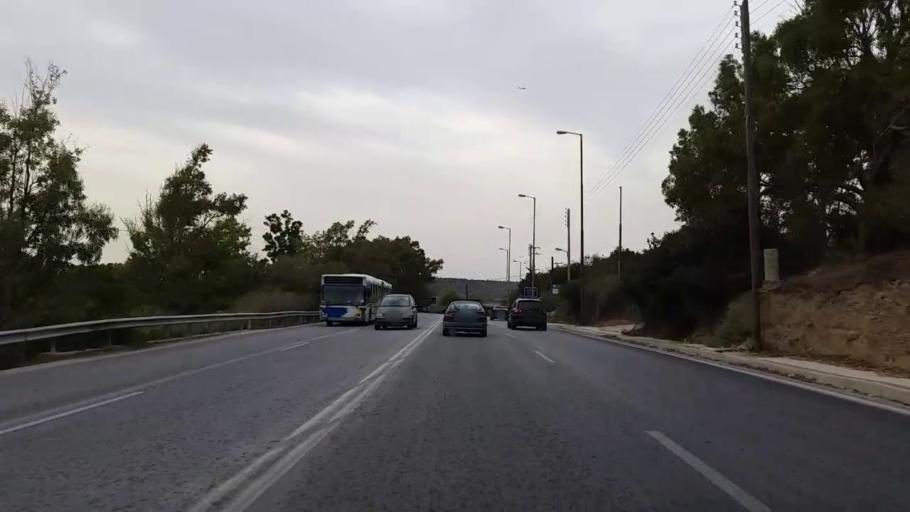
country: GR
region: Attica
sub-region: Nomarchia Anatolikis Attikis
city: Agios Dimitrios Kropias
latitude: 37.8066
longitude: 23.8521
